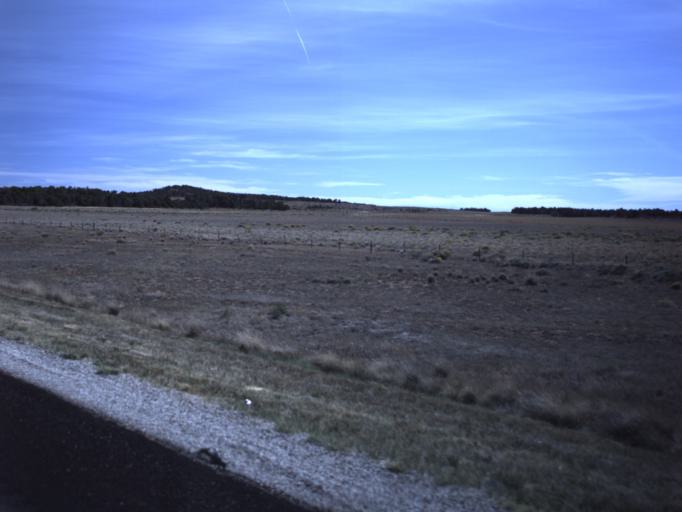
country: US
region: Colorado
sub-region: Dolores County
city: Dove Creek
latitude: 37.8341
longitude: -109.1035
